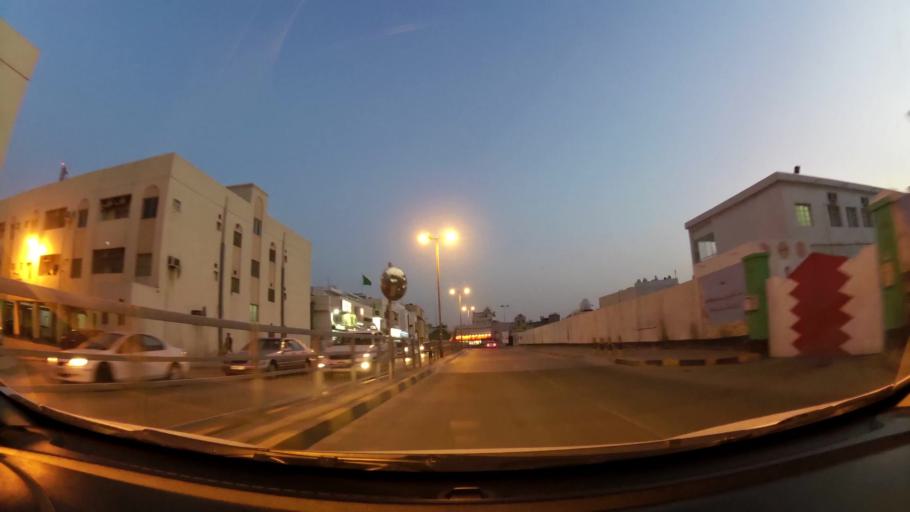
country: BH
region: Manama
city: Jidd Hafs
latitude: 26.2072
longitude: 50.5500
